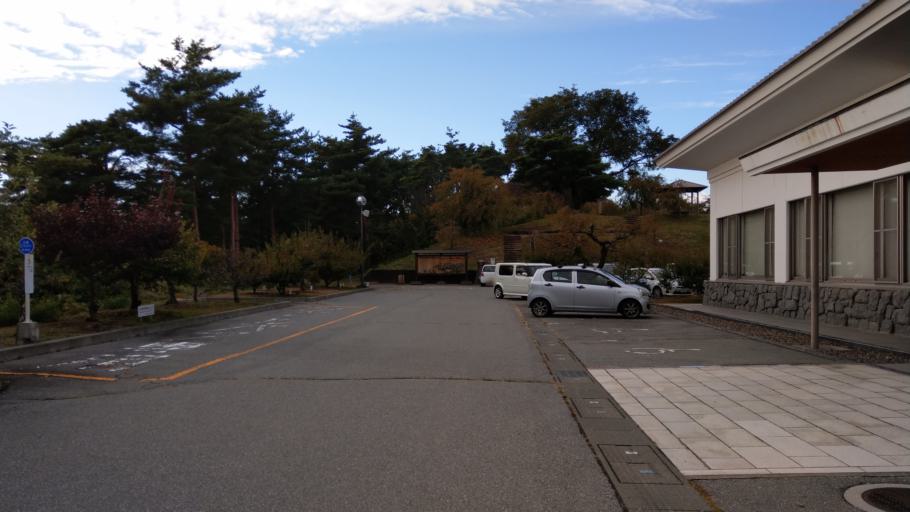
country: JP
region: Nagano
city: Komoro
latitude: 36.3437
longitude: 138.4201
